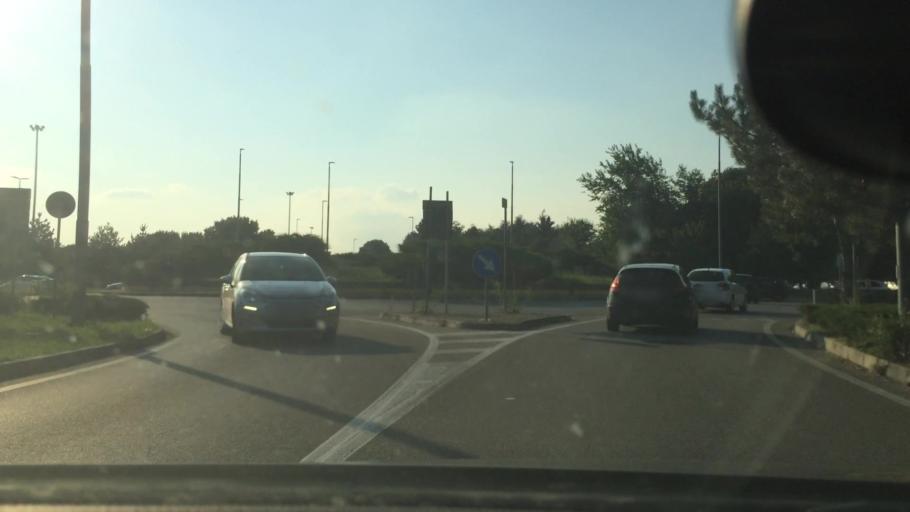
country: IT
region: Lombardy
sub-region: Citta metropolitana di Milano
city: Passirana
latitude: 45.5359
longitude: 9.0237
